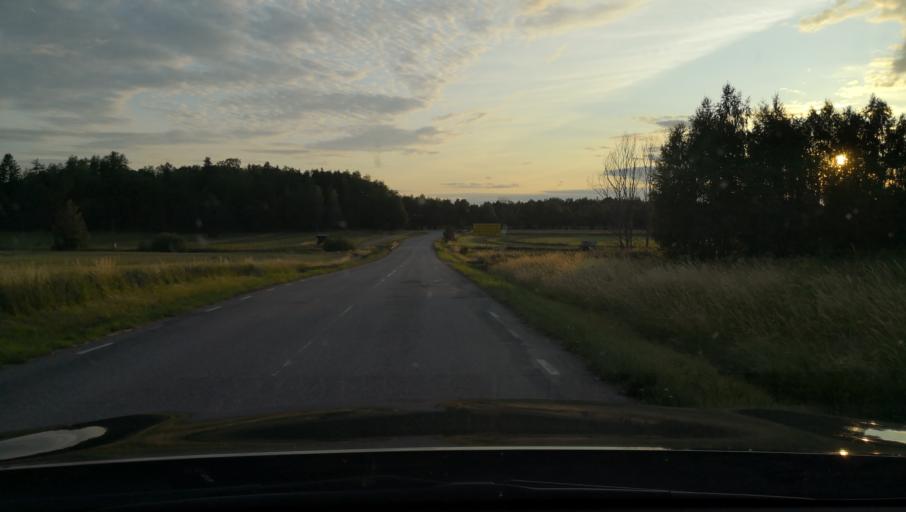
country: SE
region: Uppsala
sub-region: Uppsala Kommun
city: Vattholma
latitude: 60.0228
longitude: 17.7389
